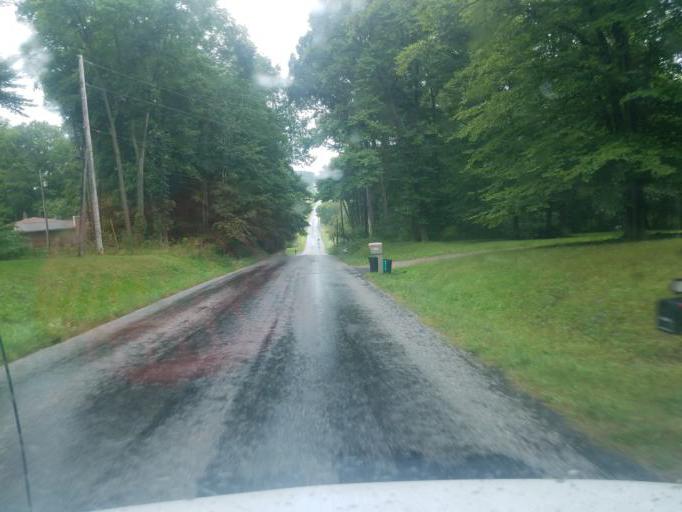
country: US
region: Ohio
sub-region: Medina County
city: Lodi
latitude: 40.9744
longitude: -82.0237
